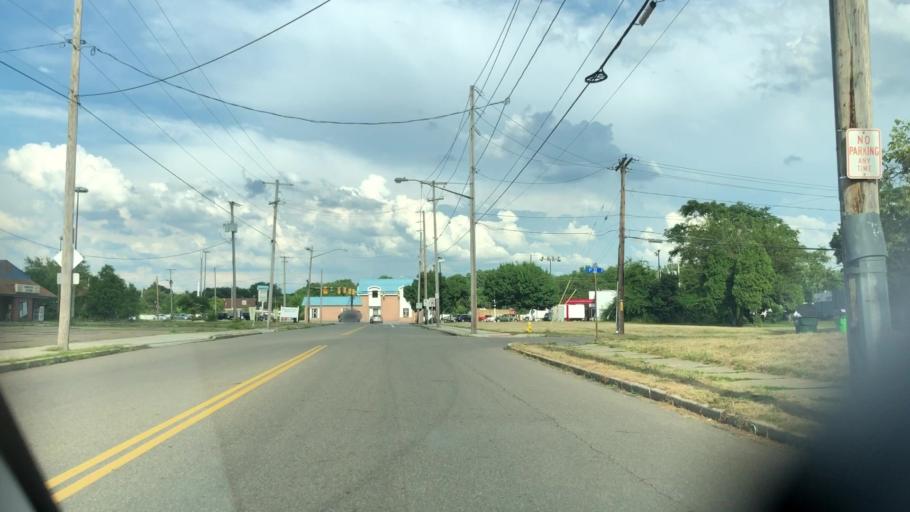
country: US
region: Ohio
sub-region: Summit County
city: Barberton
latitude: 41.0176
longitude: -81.6066
